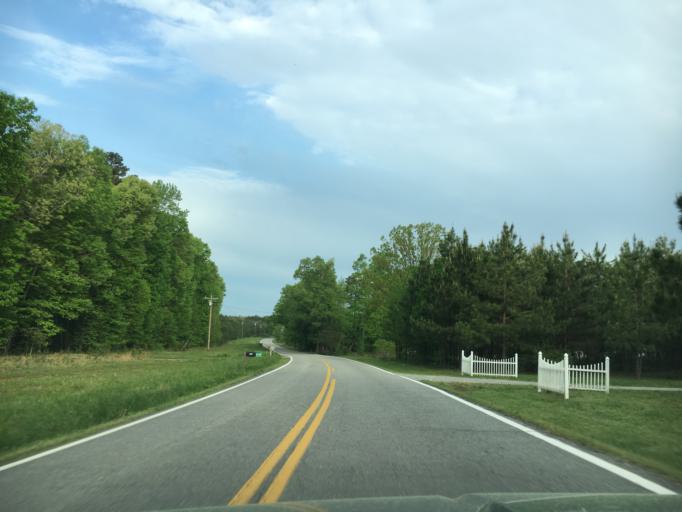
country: US
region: Virginia
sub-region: Halifax County
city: Halifax
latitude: 36.8904
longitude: -78.8055
